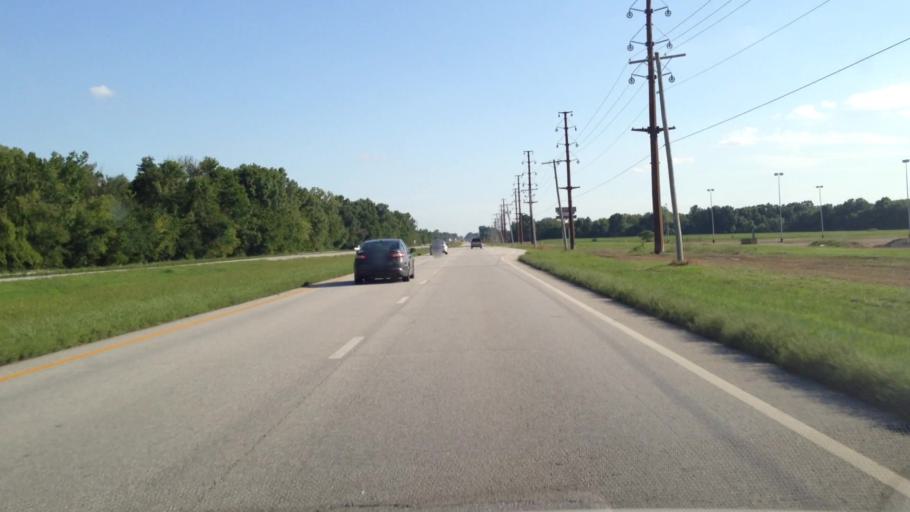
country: US
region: Kansas
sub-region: Crawford County
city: Frontenac
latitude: 37.4801
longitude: -94.7053
